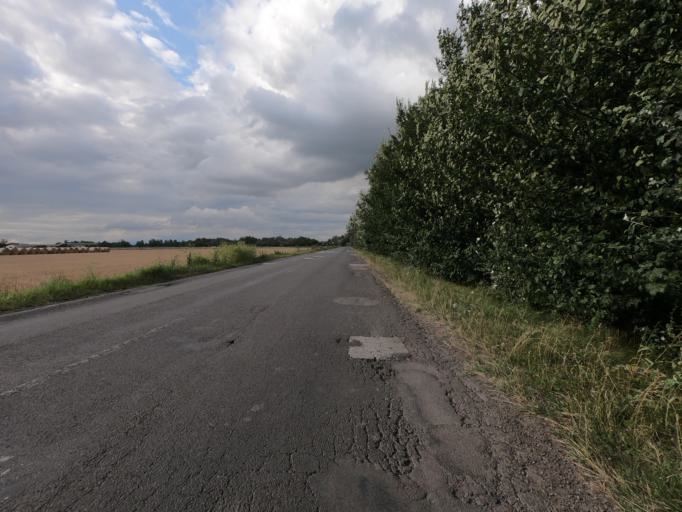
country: HU
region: Heves
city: Poroszlo
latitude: 47.6676
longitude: 20.6626
